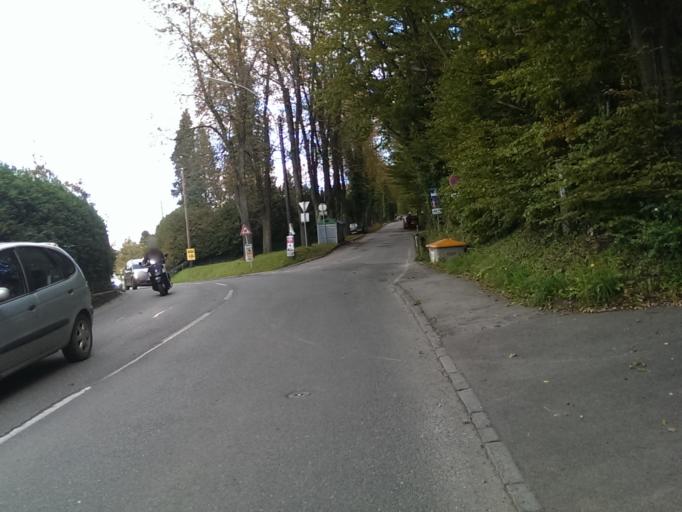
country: AT
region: Styria
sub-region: Graz Stadt
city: Mariatrost
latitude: 47.0700
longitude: 15.4910
